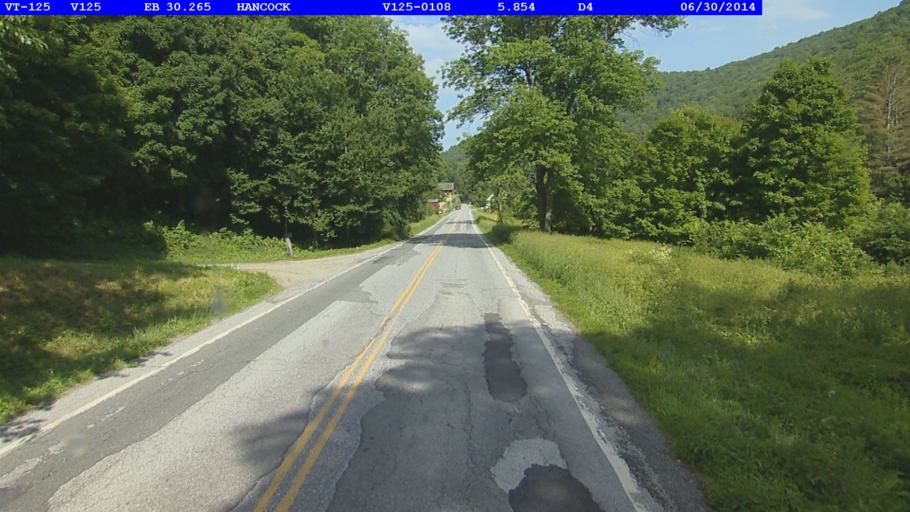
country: US
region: Vermont
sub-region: Orange County
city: Randolph
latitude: 43.9265
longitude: -72.8665
